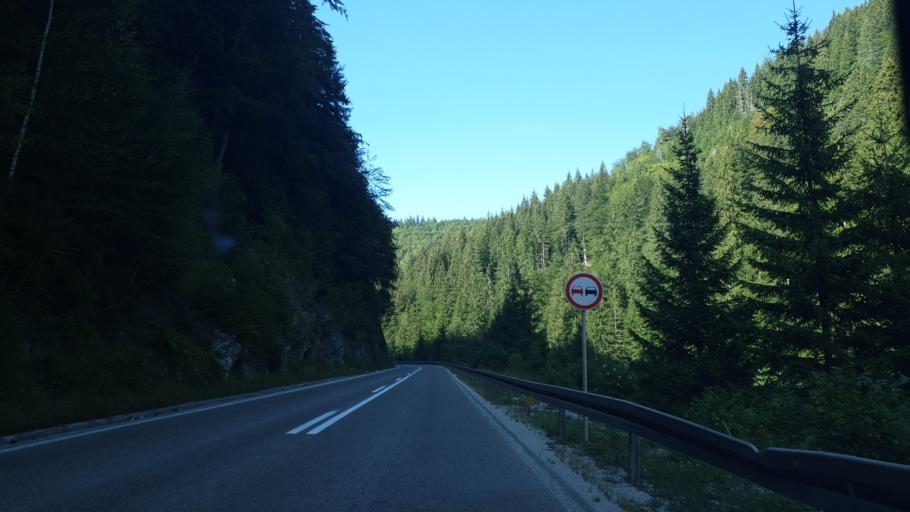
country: RS
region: Central Serbia
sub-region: Zlatiborski Okrug
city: Nova Varos
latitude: 43.4842
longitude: 19.8267
